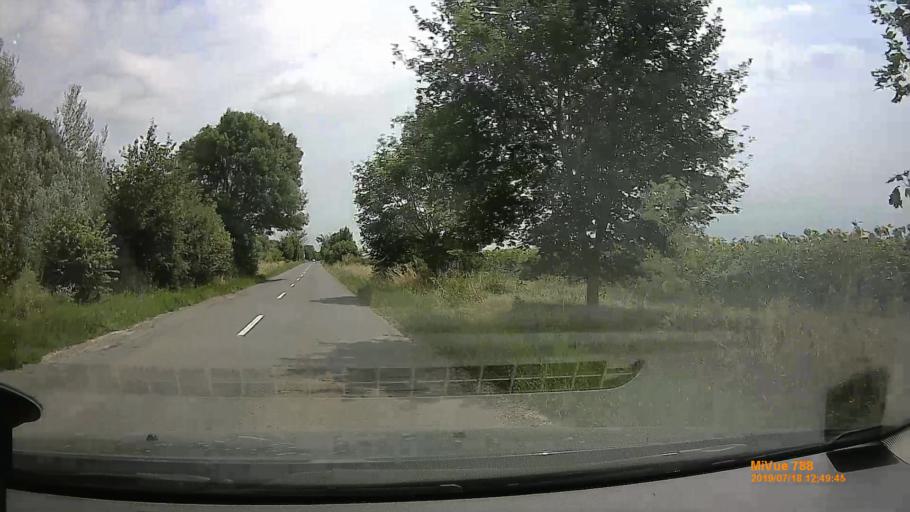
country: HU
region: Pest
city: Perbal
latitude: 47.5736
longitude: 18.7828
